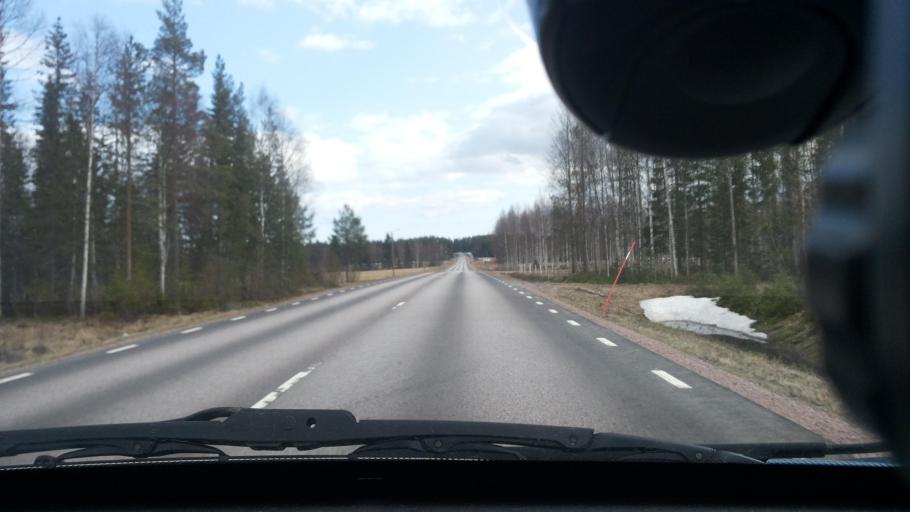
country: SE
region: Norrbotten
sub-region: Lulea Kommun
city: Sodra Sunderbyn
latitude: 65.6146
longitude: 21.9505
